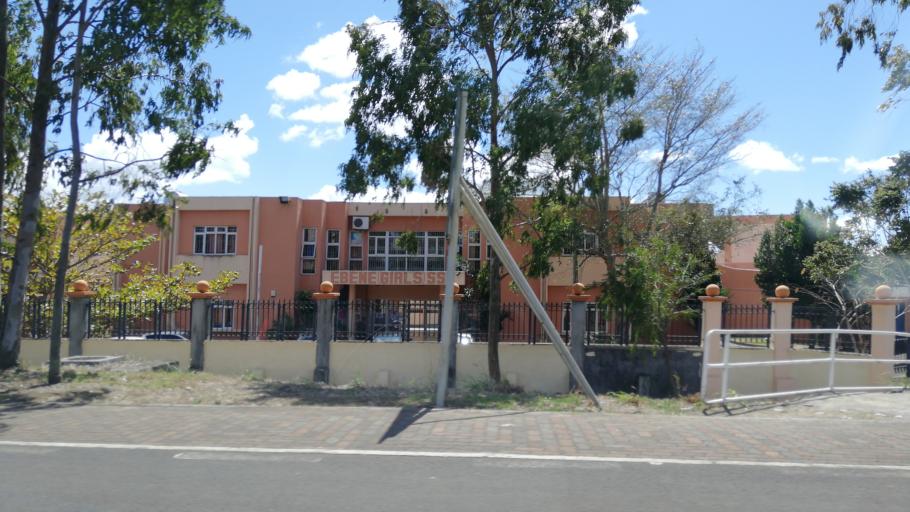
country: MU
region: Plaines Wilhems
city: Ebene
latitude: -20.2392
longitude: 57.4792
